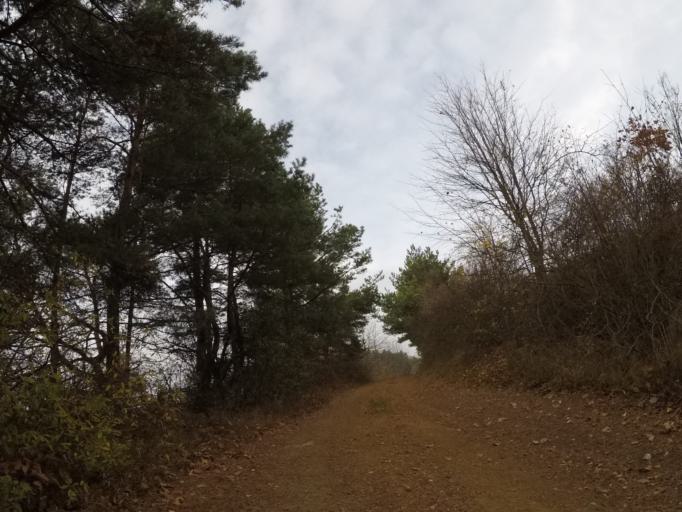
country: SK
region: Presovsky
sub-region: Okres Presov
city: Presov
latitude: 48.9251
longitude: 21.1424
